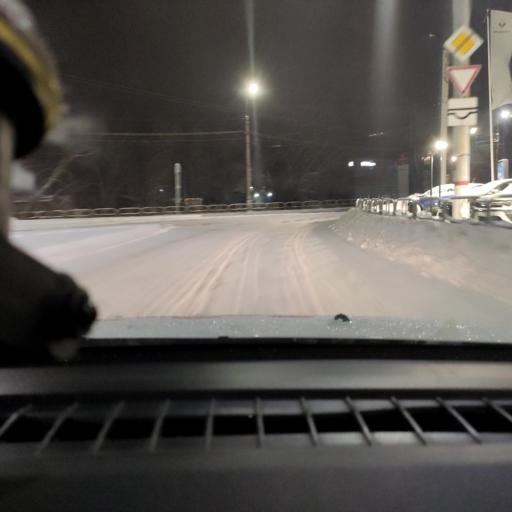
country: RU
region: Samara
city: Novokuybyshevsk
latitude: 53.0863
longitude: 49.9481
